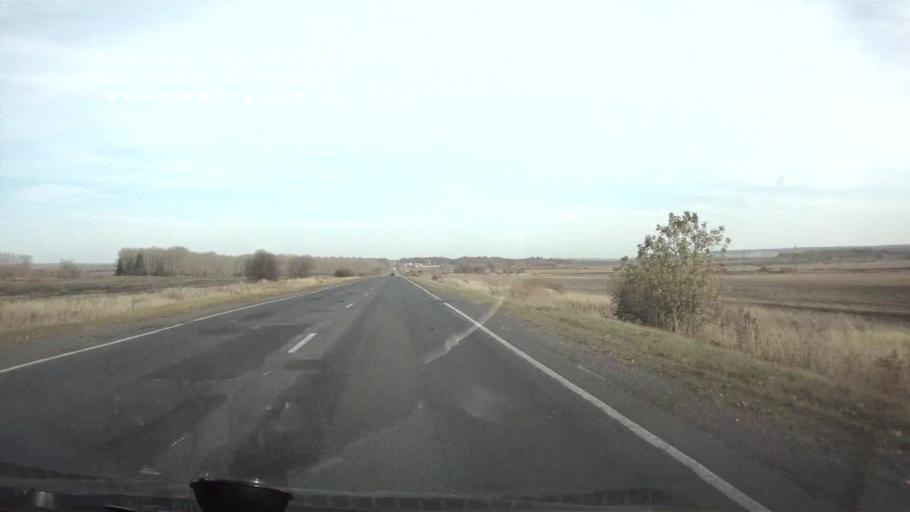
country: RU
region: Mordoviya
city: Atyashevo
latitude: 54.5473
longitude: 45.9490
